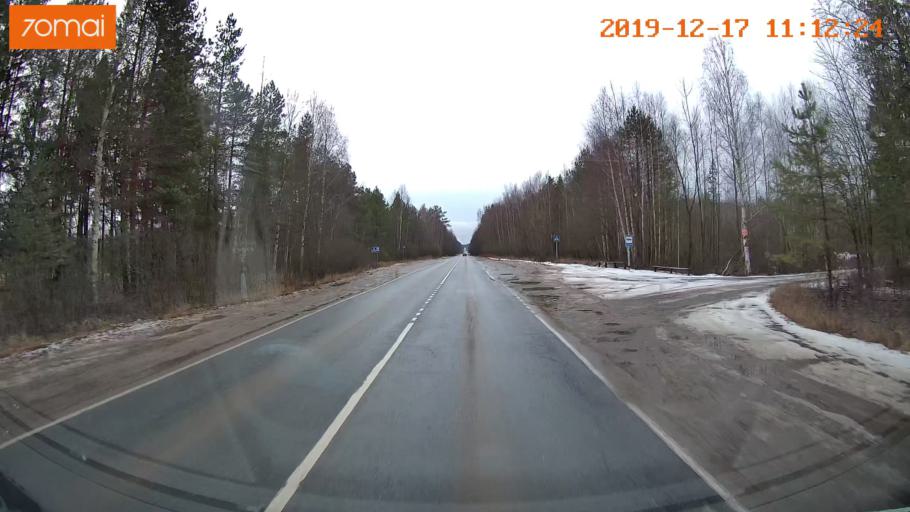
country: RU
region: Vladimir
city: Gus'-Khrustal'nyy
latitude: 55.5762
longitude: 40.6287
